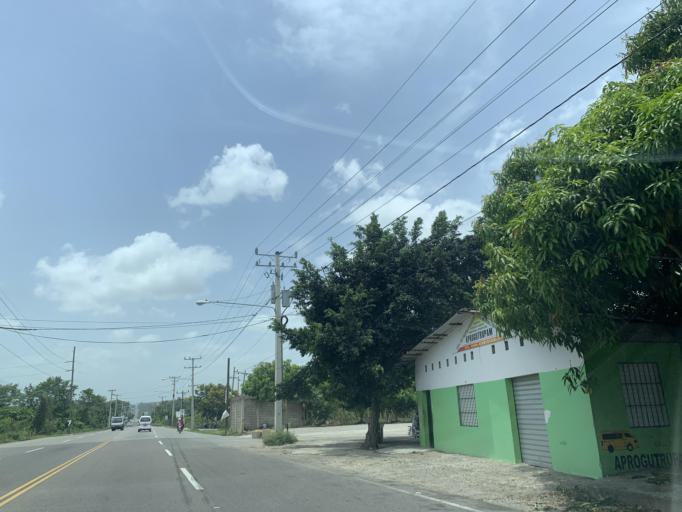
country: DO
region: Puerto Plata
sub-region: Puerto Plata
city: Puerto Plata
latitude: 19.7541
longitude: -70.6423
